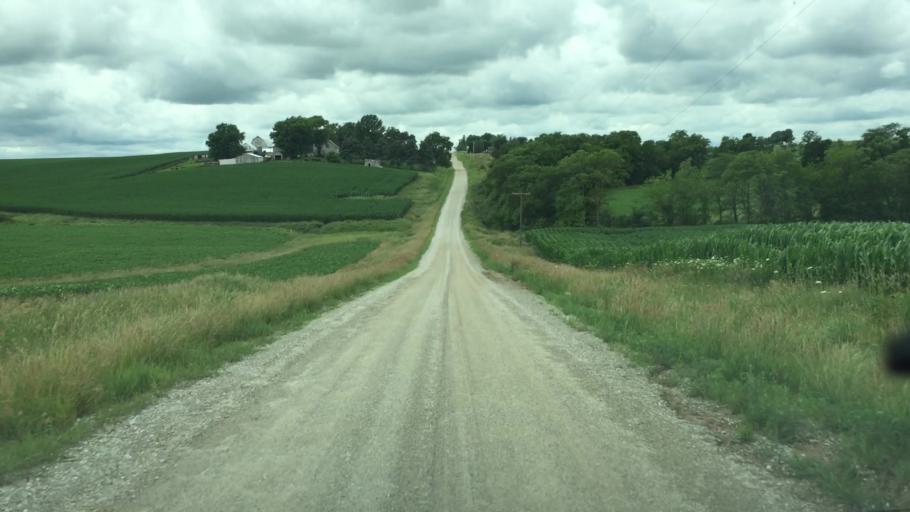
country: US
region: Iowa
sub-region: Jasper County
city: Monroe
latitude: 41.6009
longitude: -93.1412
